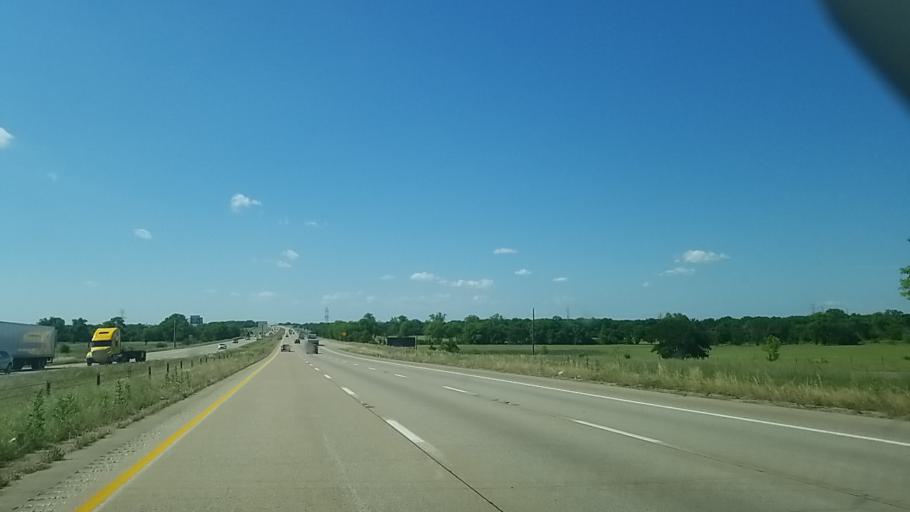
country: US
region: Texas
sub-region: Ellis County
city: Ferris
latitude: 32.5502
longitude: -96.6607
